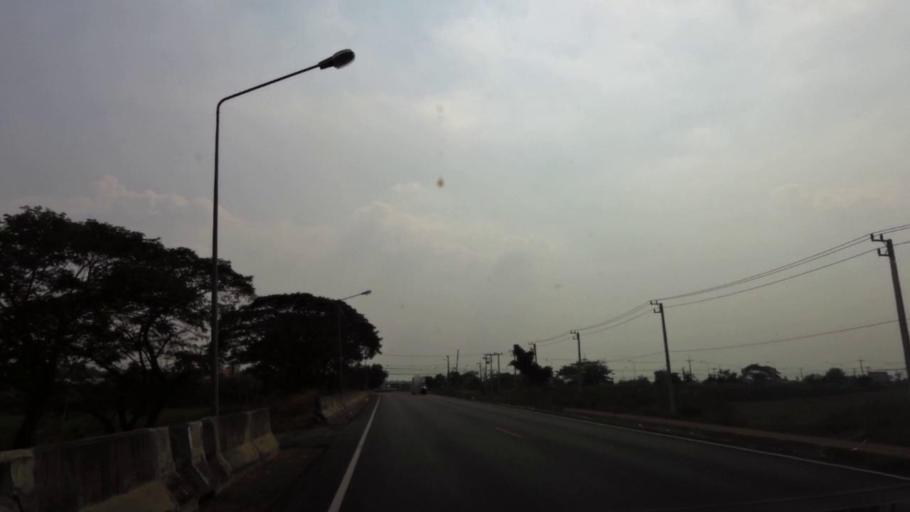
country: TH
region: Phra Nakhon Si Ayutthaya
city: Phra Nakhon Si Ayutthaya
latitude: 14.3062
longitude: 100.5625
